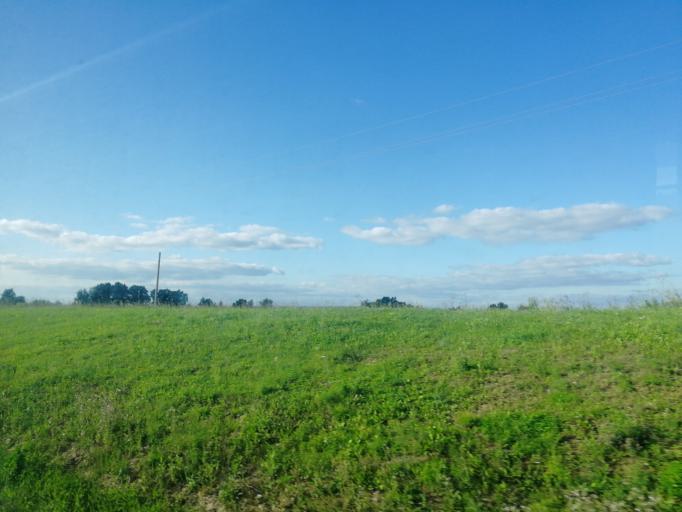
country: RU
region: Tula
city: Leninskiy
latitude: 54.2445
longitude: 37.3292
